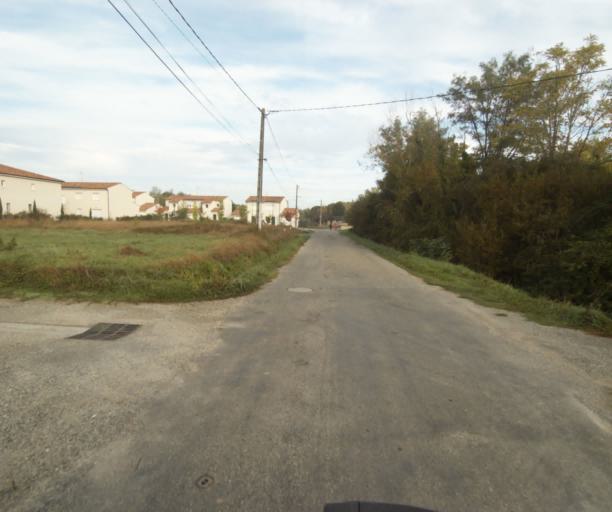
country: FR
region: Midi-Pyrenees
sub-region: Departement du Tarn-et-Garonne
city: Montech
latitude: 43.9673
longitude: 1.2282
